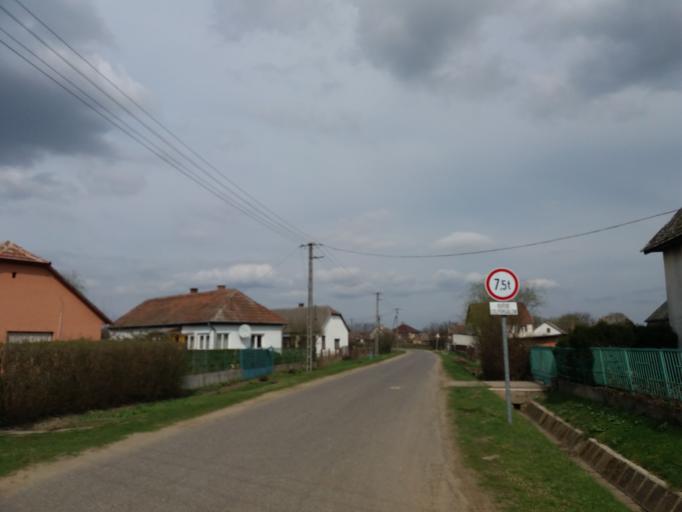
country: HU
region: Szabolcs-Szatmar-Bereg
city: Petnehaza
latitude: 48.0599
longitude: 22.0435
